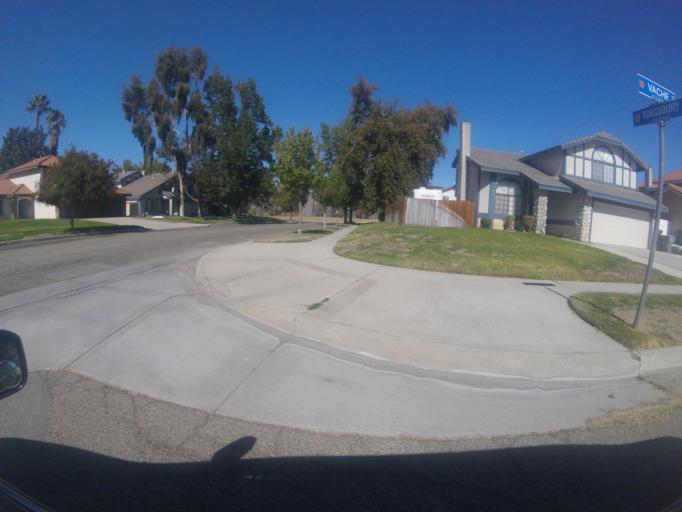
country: US
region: California
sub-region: San Bernardino County
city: Redlands
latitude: 34.0831
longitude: -117.1764
